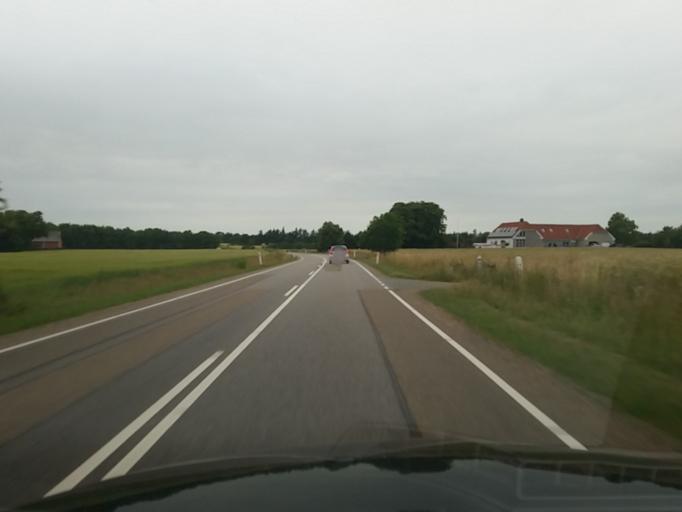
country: DK
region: South Denmark
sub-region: Billund Kommune
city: Grindsted
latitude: 55.6608
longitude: 8.7772
